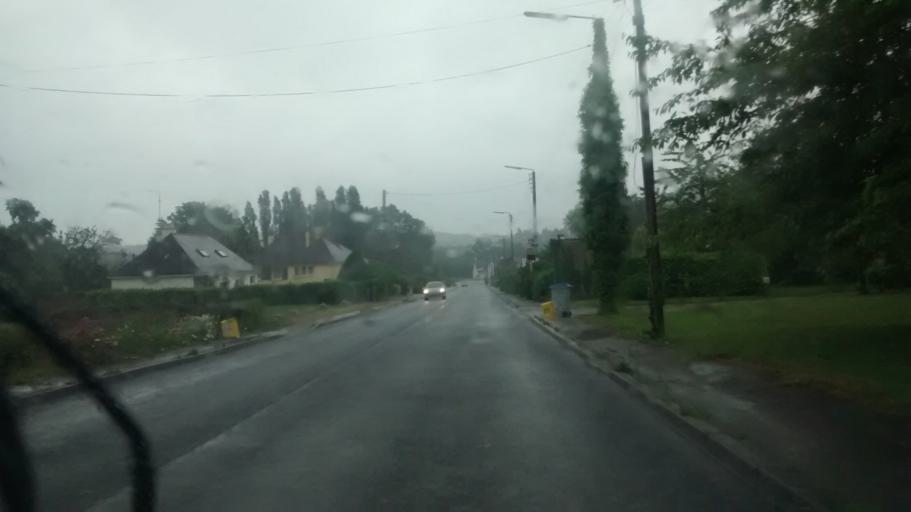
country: FR
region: Brittany
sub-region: Departement du Morbihan
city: La Gacilly
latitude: 47.7688
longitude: -2.1415
